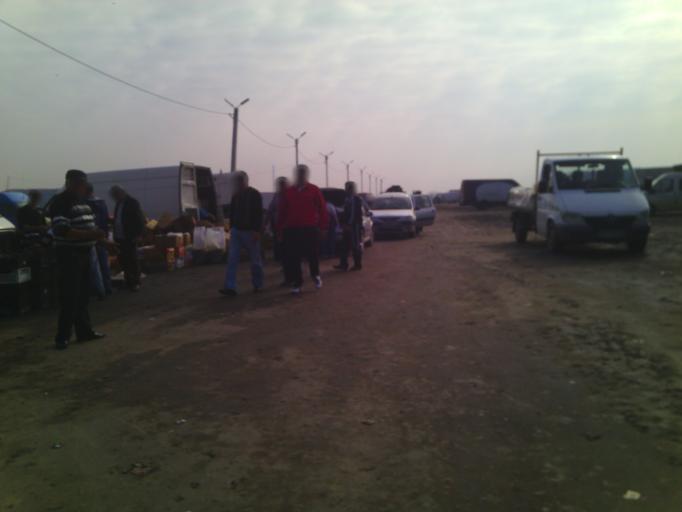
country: RO
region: Ilfov
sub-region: Comuna Magurele
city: Magurele
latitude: 44.3840
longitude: 26.0598
